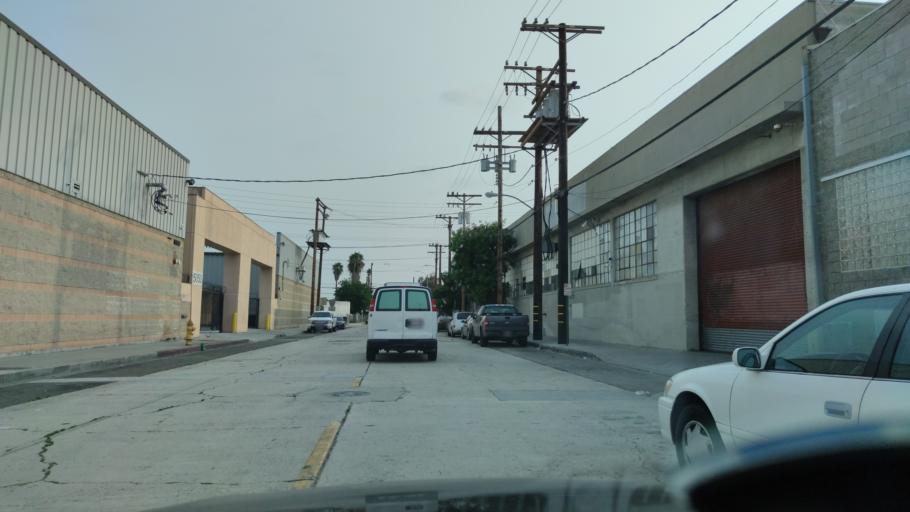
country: US
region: California
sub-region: Los Angeles County
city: Maywood
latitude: 33.9973
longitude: -118.1996
